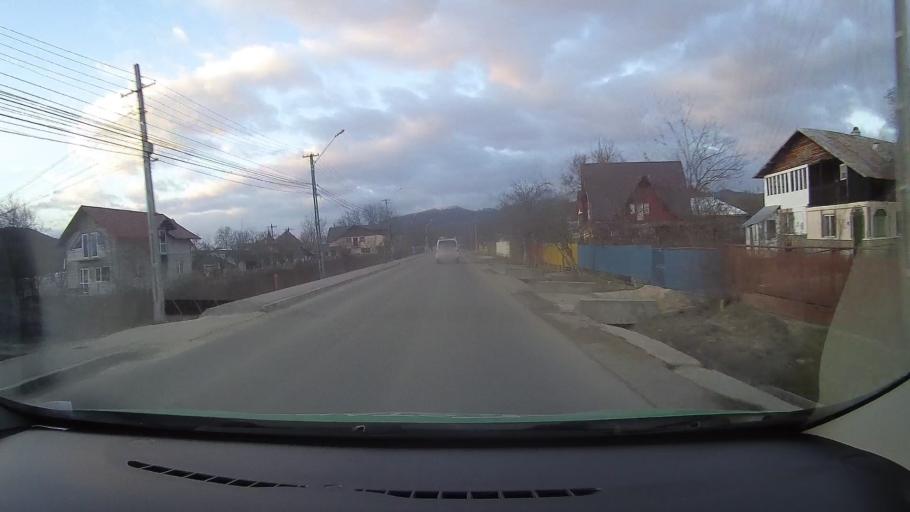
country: RO
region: Dambovita
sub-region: Municipiul Moreni
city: Moreni
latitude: 45.0026
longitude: 25.6468
